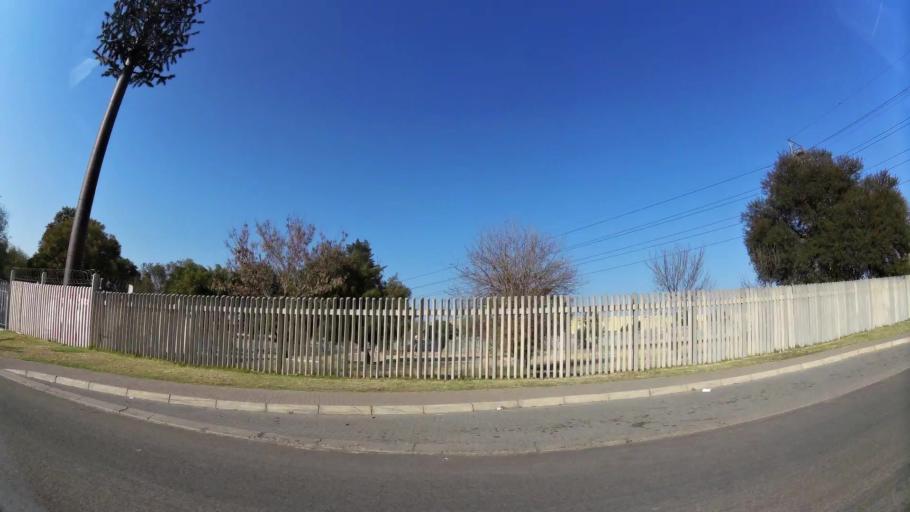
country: ZA
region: Gauteng
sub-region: Ekurhuleni Metropolitan Municipality
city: Boksburg
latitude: -26.2341
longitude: 28.2326
